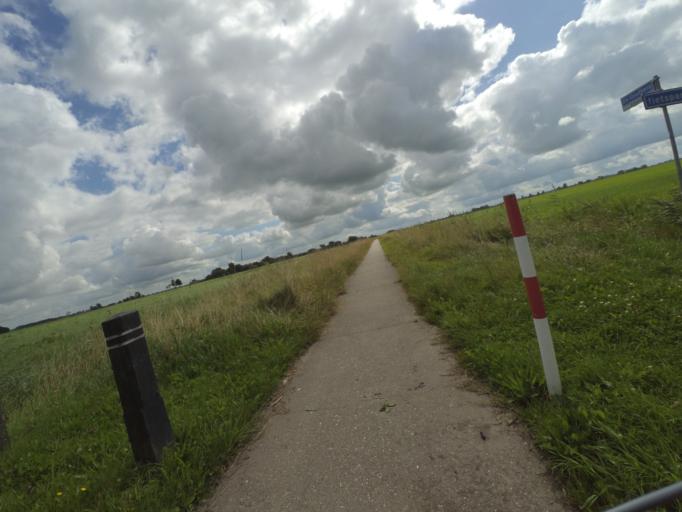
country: NL
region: Friesland
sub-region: Gemeente Kollumerland en Nieuwkruisland
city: Kollum
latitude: 53.2721
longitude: 6.1790
